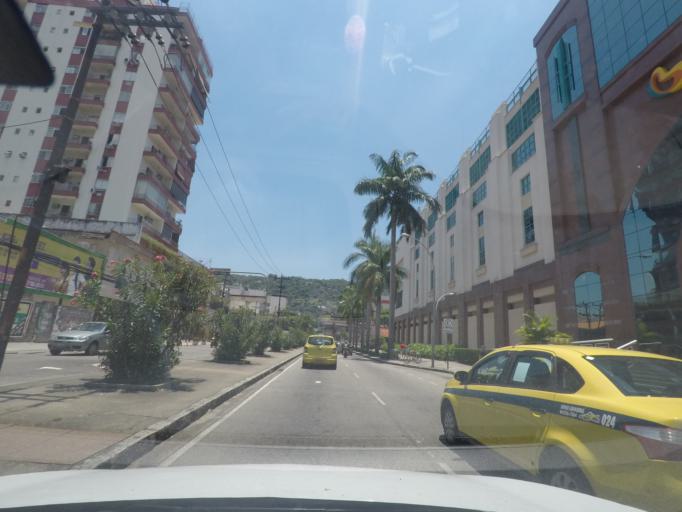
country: BR
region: Rio de Janeiro
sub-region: Rio De Janeiro
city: Rio de Janeiro
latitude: -22.9195
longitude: -43.2507
